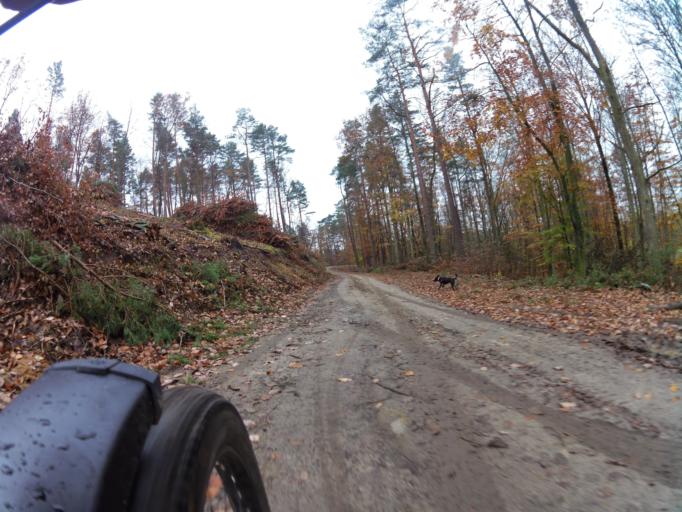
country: PL
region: Pomeranian Voivodeship
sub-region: Powiat pucki
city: Krokowa
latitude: 54.7496
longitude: 18.0909
